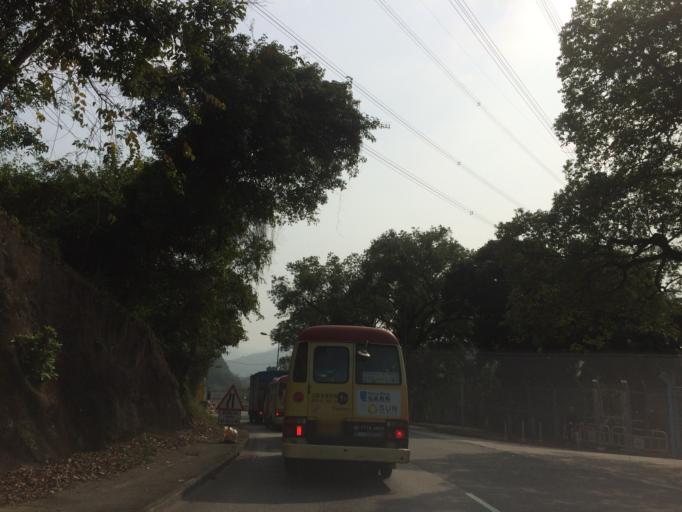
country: HK
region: Tai Po
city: Tai Po
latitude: 22.4607
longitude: 114.1486
